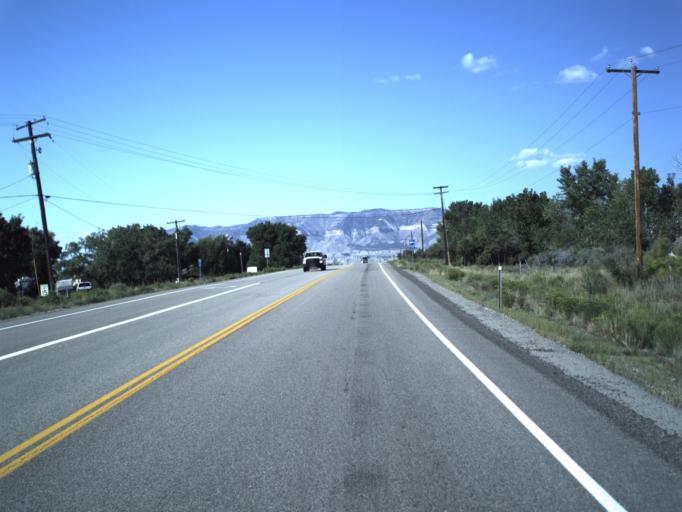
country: US
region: Utah
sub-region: Emery County
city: Ferron
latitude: 39.1281
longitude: -111.1041
